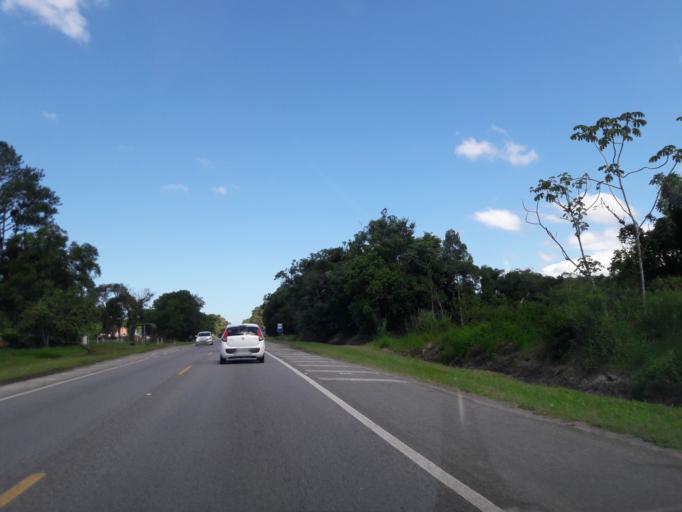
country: BR
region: Parana
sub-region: Paranagua
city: Paranagua
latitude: -25.5960
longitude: -48.5609
